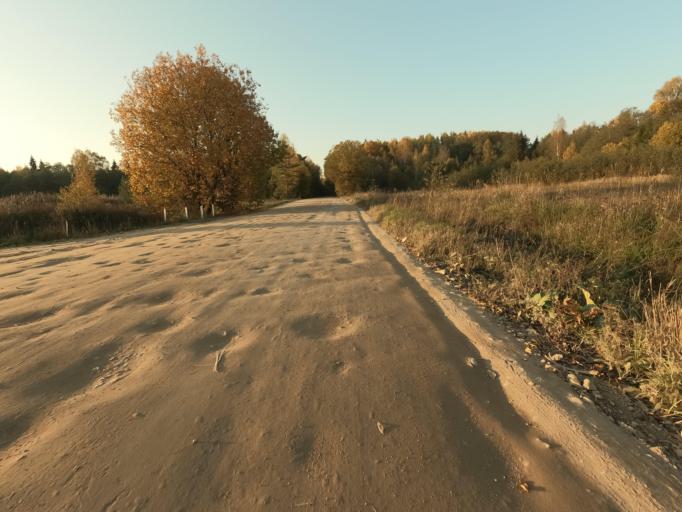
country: RU
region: Leningrad
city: Lyuban'
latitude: 59.0107
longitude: 31.0902
